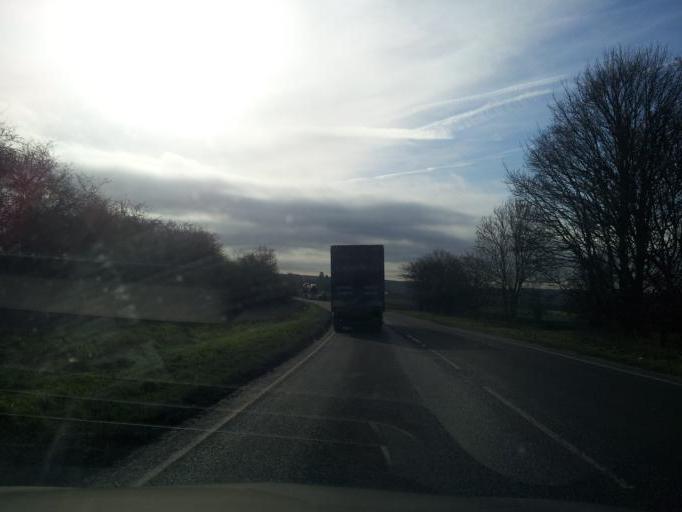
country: GB
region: England
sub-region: District of Rutland
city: Ketton
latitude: 52.6073
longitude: -0.5357
